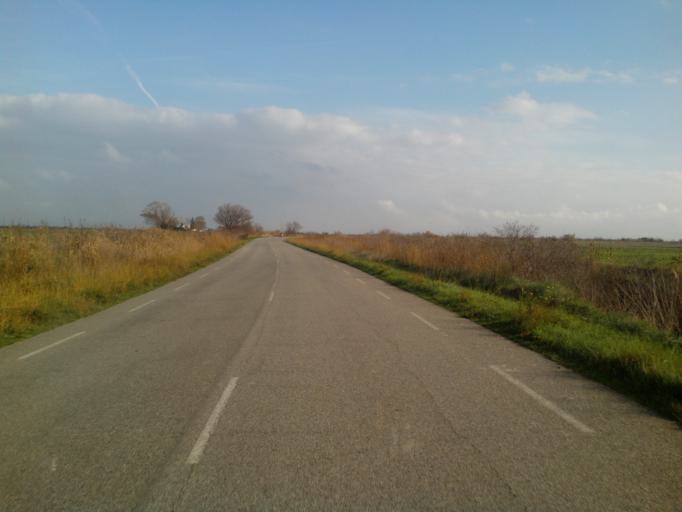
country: FR
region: Languedoc-Roussillon
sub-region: Departement du Gard
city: Saint-Gilles
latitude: 43.6055
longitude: 4.4838
